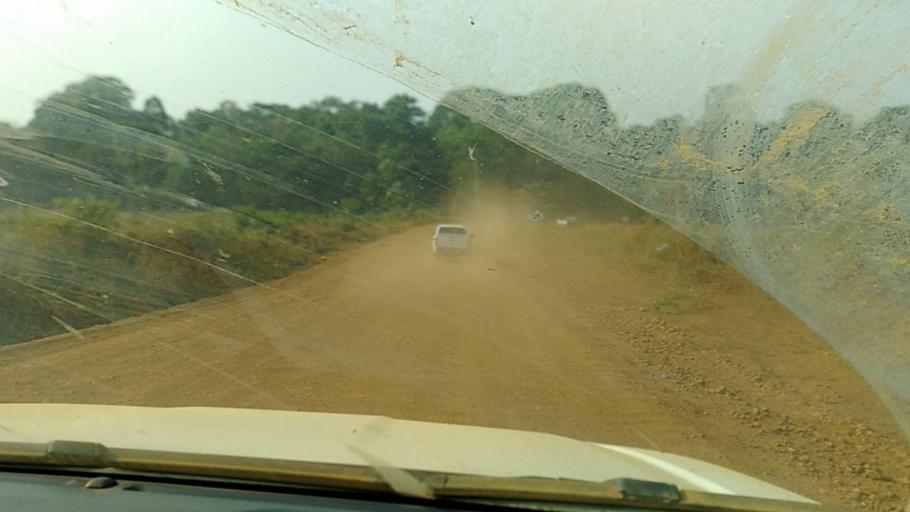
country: BR
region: Rondonia
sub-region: Porto Velho
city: Porto Velho
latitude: -8.7574
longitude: -63.9613
